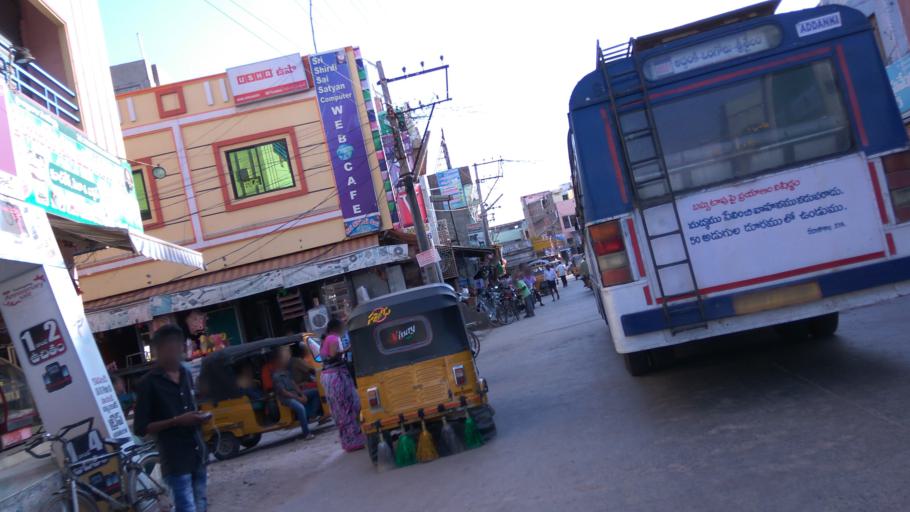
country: IN
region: Andhra Pradesh
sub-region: Prakasam
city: Markapur
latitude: 15.7401
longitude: 79.2722
